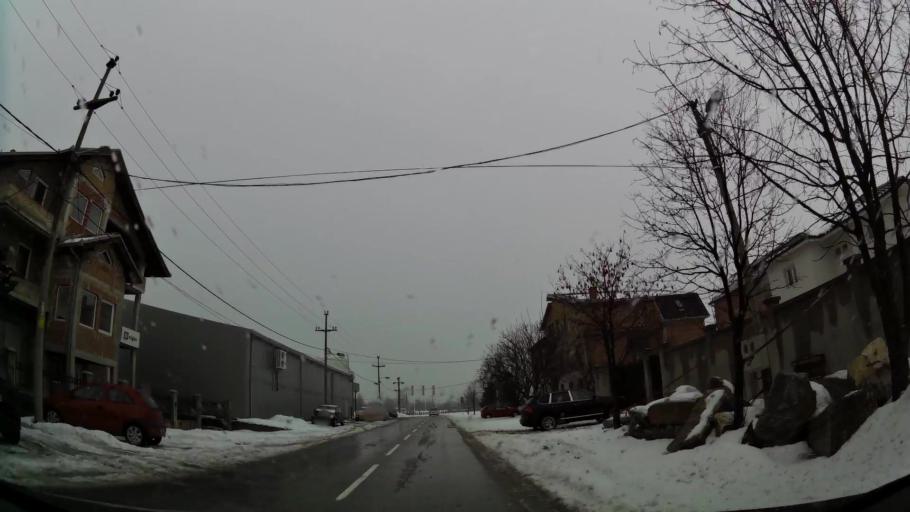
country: RS
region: Central Serbia
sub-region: Belgrade
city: Zemun
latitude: 44.8462
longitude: 20.3464
